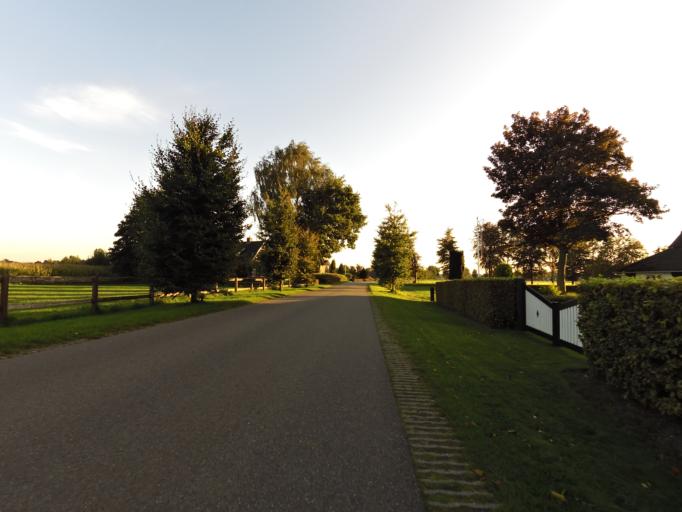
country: NL
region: Gelderland
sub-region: Gemeente Doesburg
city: Doesburg
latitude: 51.9439
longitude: 6.1594
